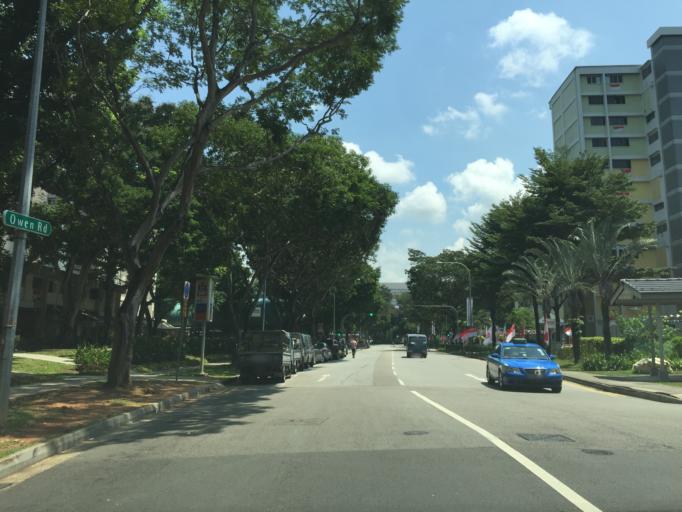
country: SG
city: Singapore
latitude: 1.3155
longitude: 103.8514
